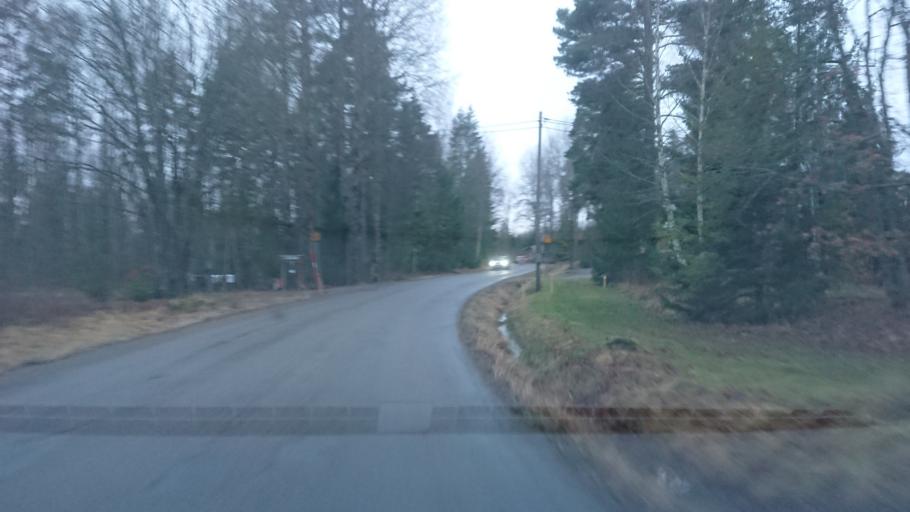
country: SE
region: Uppsala
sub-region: Osthammars Kommun
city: Bjorklinge
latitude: 59.9971
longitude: 17.5962
